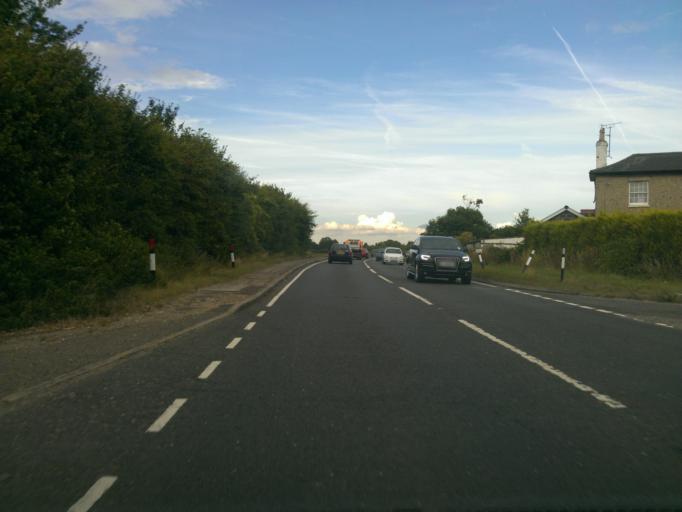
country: GB
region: England
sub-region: Essex
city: Coggeshall
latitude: 51.8737
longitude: 0.7145
